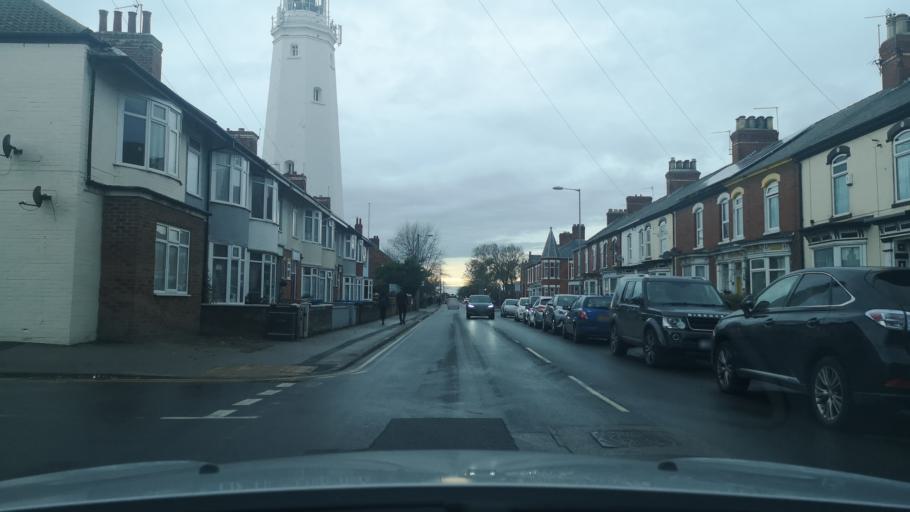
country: GB
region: England
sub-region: East Riding of Yorkshire
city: Withernsea
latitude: 53.7312
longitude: 0.0298
